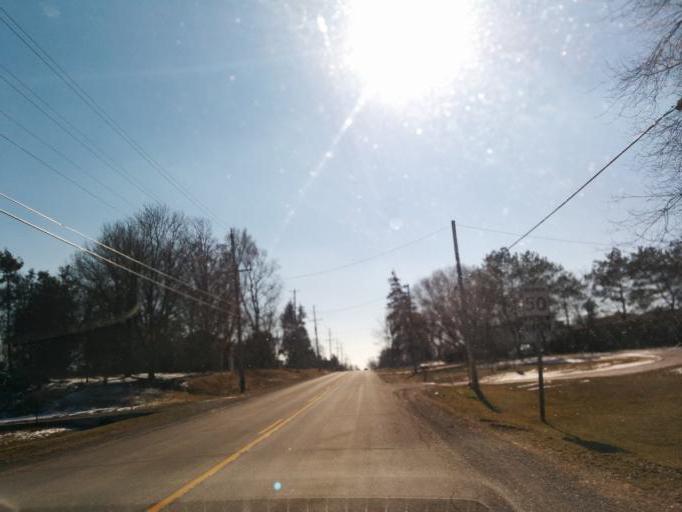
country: CA
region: Ontario
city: Brant
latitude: 43.0354
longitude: -80.3324
